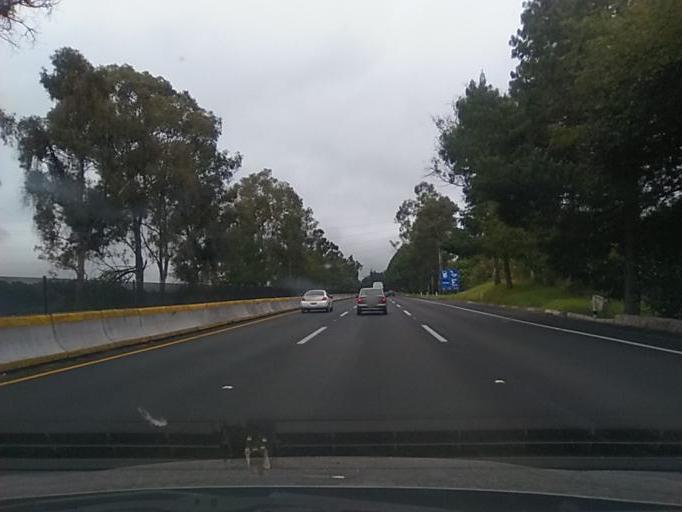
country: MX
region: Mexico City
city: Xochimilco
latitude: 19.1872
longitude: -99.1575
